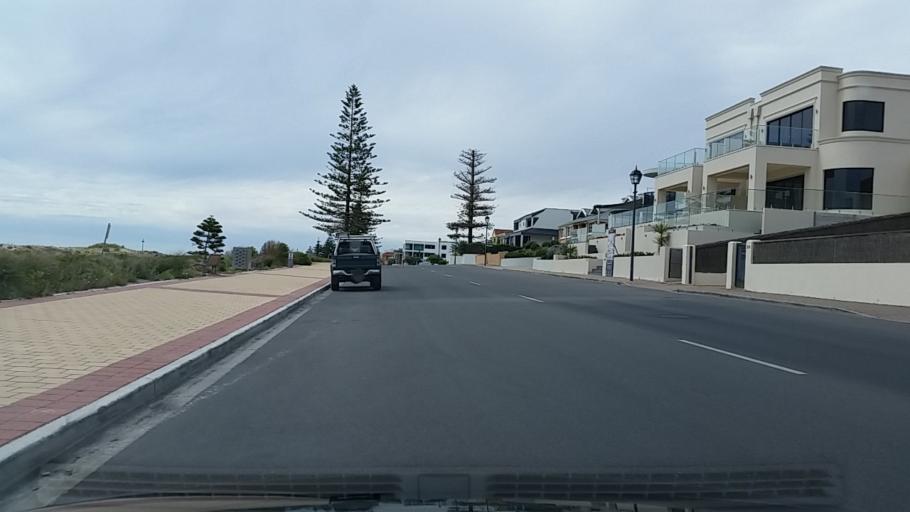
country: AU
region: South Australia
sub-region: Adelaide Hills
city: Seacliff
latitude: -35.0301
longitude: 138.5177
